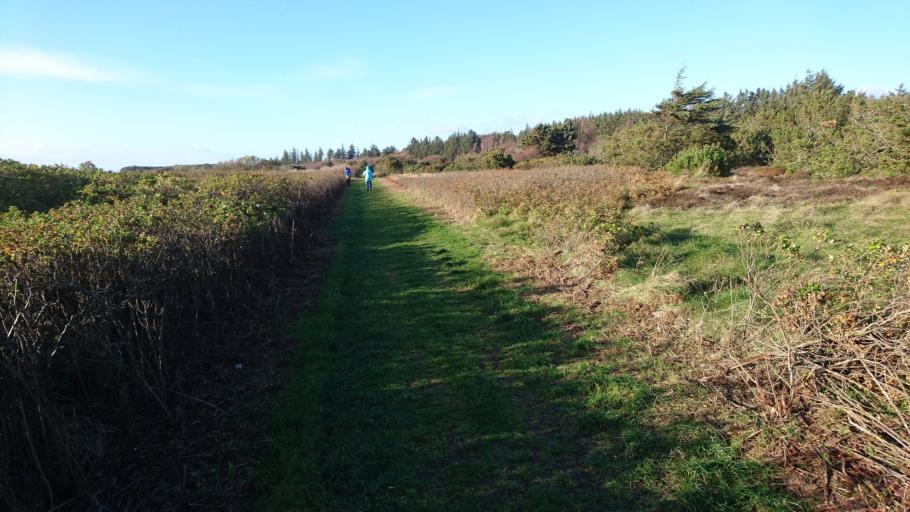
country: DK
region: North Denmark
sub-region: Morso Kommune
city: Nykobing Mors
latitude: 56.8299
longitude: 8.9617
